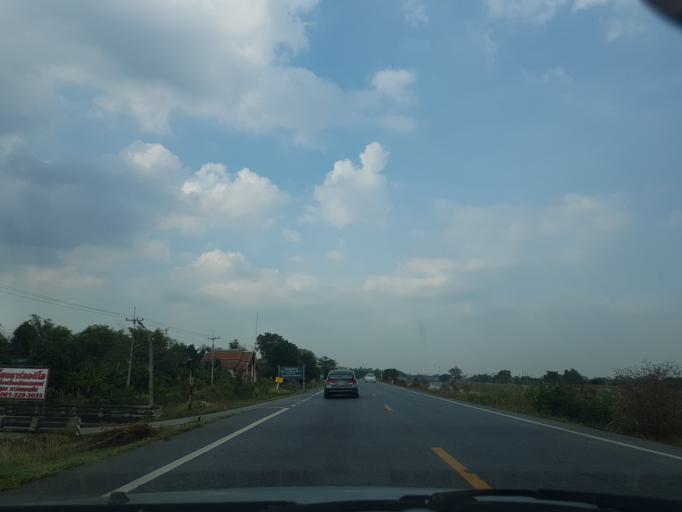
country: TH
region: Phra Nakhon Si Ayutthaya
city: Phachi
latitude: 14.4889
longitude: 100.7374
